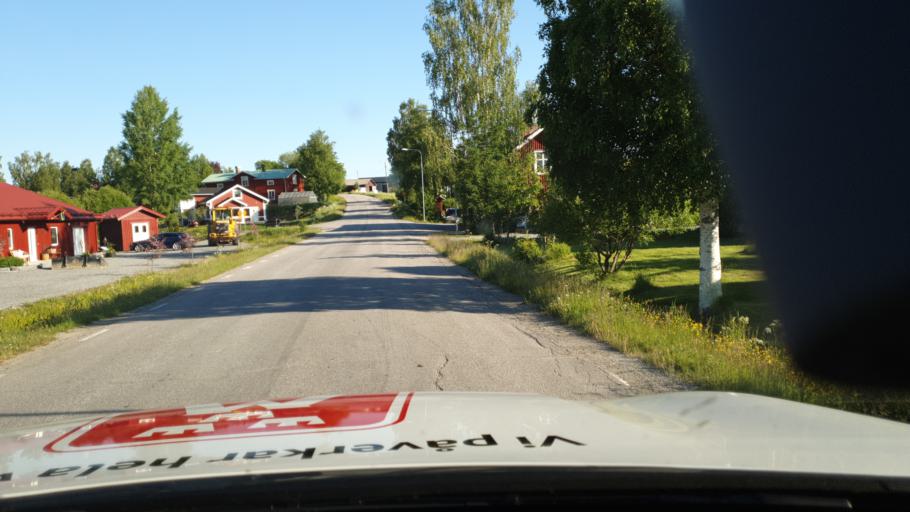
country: SE
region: Vaesterbotten
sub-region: Umea Kommun
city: Roback
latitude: 64.0368
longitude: 20.0780
